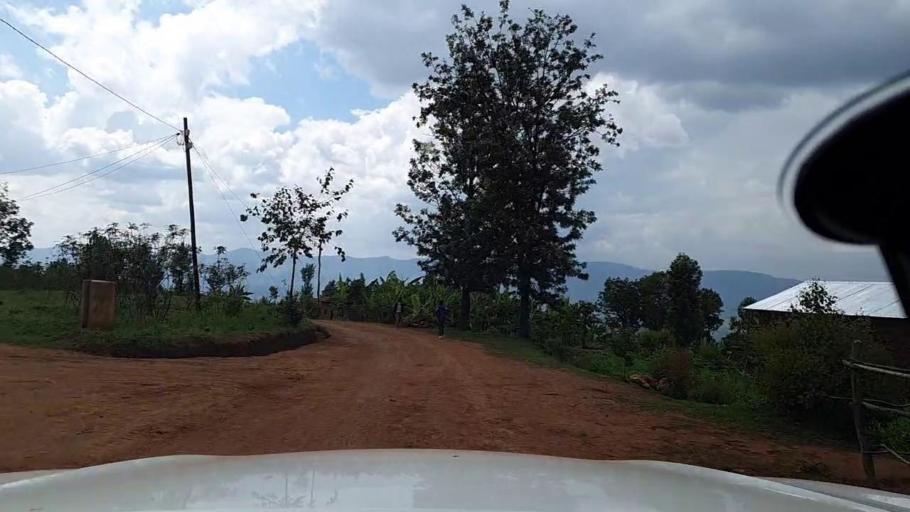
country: RW
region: Southern Province
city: Gitarama
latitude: -1.8380
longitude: 29.8296
